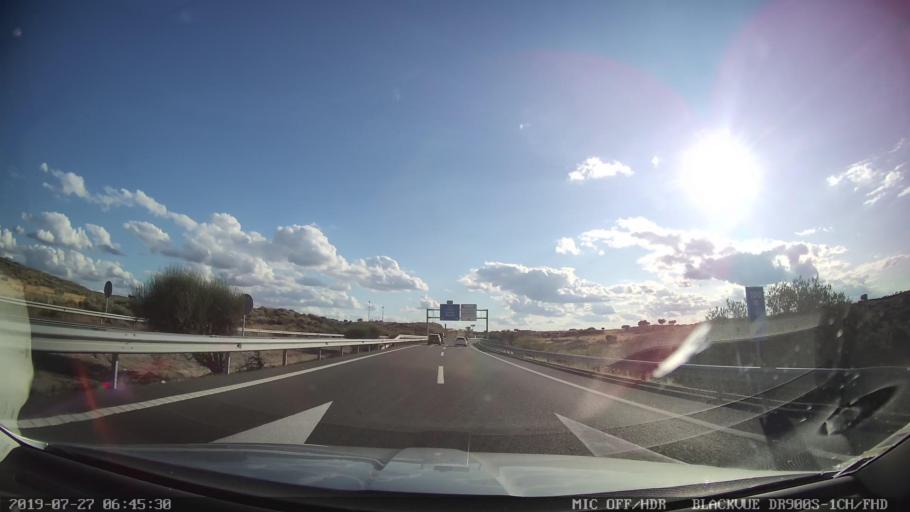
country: ES
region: Extremadura
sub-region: Provincia de Caceres
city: Navalmoral de la Mata
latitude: 39.8772
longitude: -5.5425
